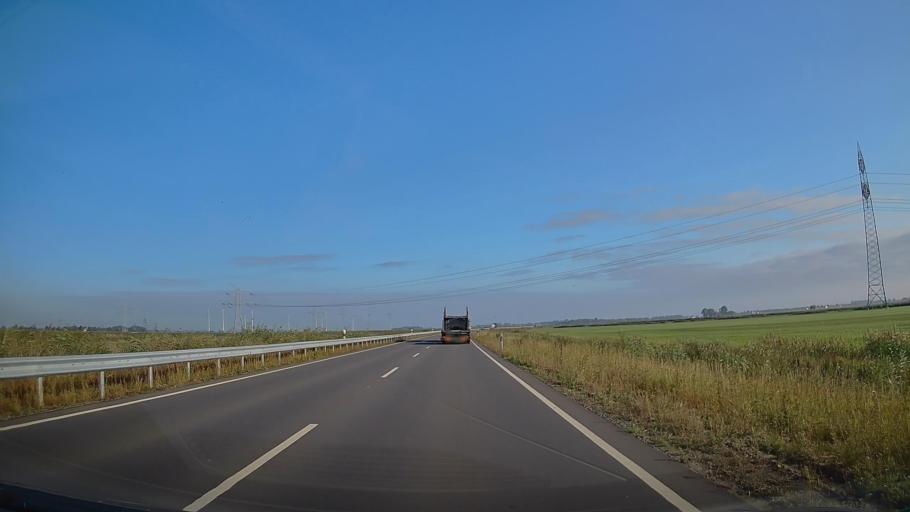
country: DE
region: Lower Saxony
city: Ovelgonne
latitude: 53.3150
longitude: 8.4006
